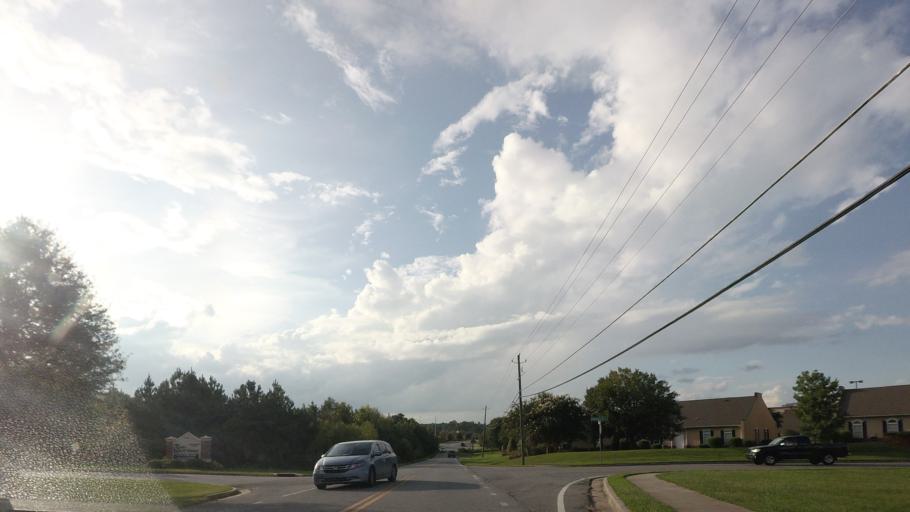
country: US
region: Georgia
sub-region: Bibb County
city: West Point
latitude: 32.8761
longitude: -83.7619
